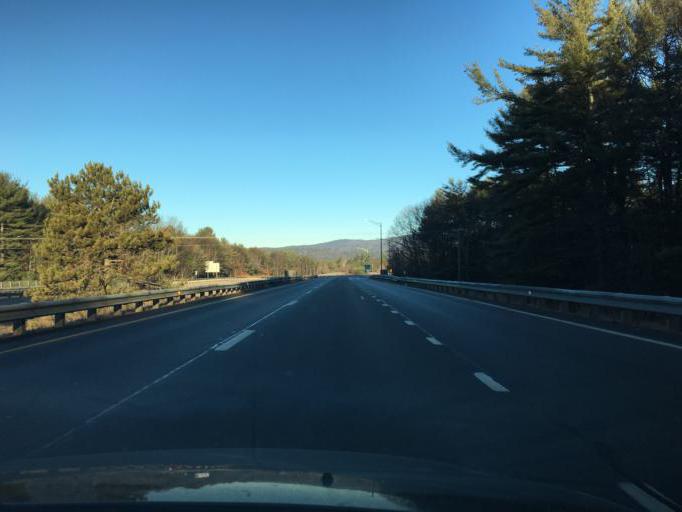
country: US
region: New Hampshire
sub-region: Belknap County
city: Sanbornton
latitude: 43.5041
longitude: -71.6147
